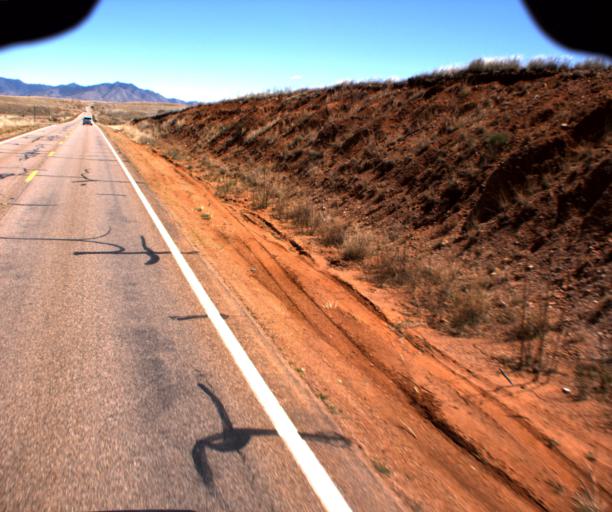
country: US
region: Arizona
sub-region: Cochise County
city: Huachuca City
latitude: 31.6998
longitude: -110.5936
